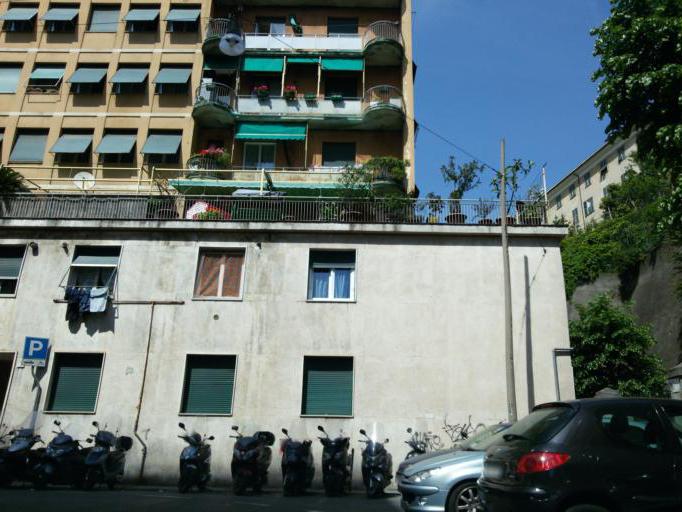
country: IT
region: Liguria
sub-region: Provincia di Genova
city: Genoa
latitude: 44.4170
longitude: 8.9589
